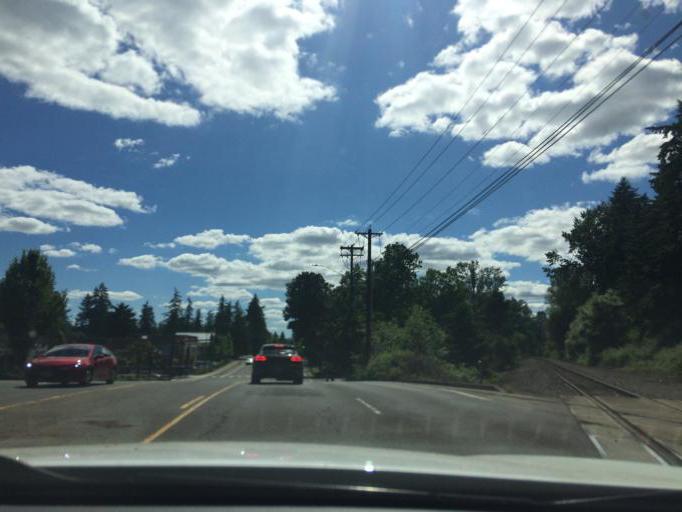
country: US
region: Oregon
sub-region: Washington County
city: Durham
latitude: 45.4028
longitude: -122.7326
